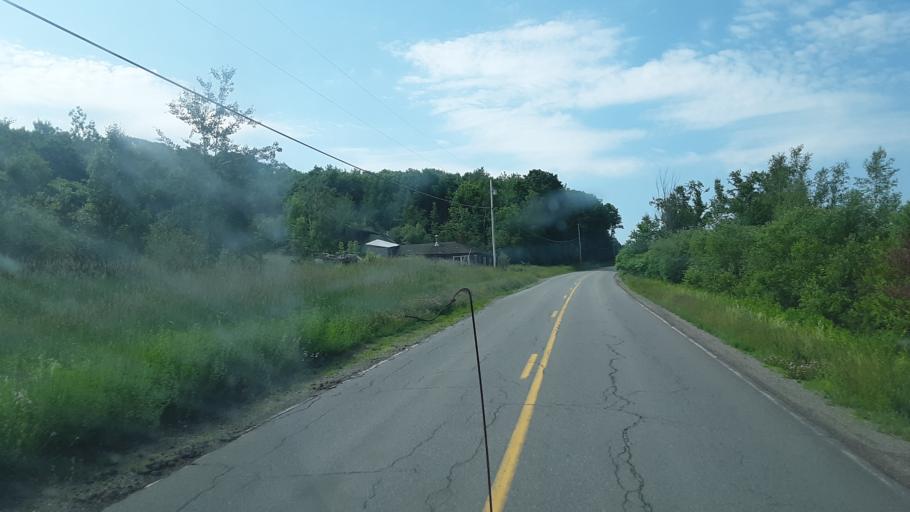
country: US
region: Maine
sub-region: Waldo County
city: Frankfort
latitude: 44.5910
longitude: -68.9438
